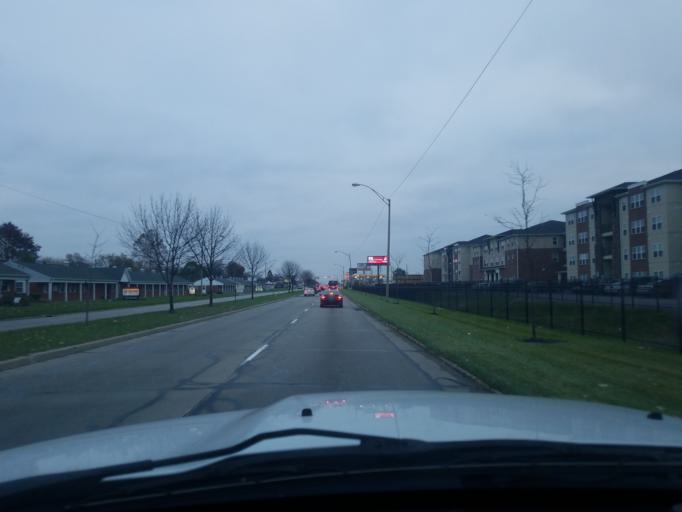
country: US
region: Indiana
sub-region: Delaware County
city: Muncie
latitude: 40.2189
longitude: -85.4130
